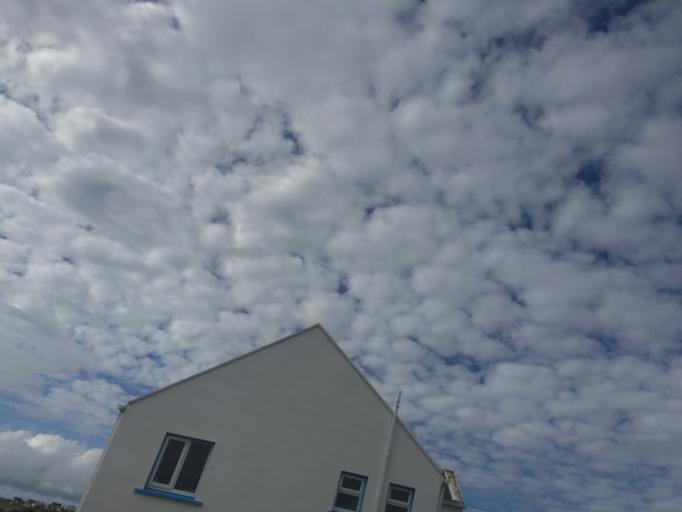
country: IE
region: Ulster
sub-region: County Donegal
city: Derrybeg
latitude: 55.2552
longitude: -8.1954
